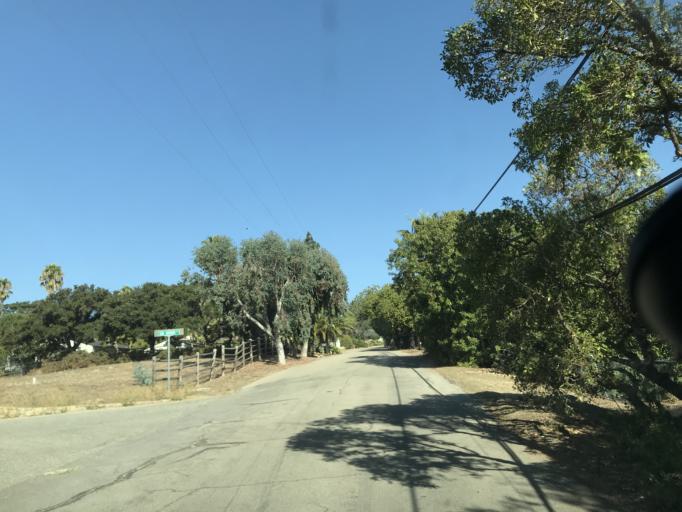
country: US
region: California
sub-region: Santa Barbara County
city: Goleta
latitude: 34.4547
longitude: -119.7861
